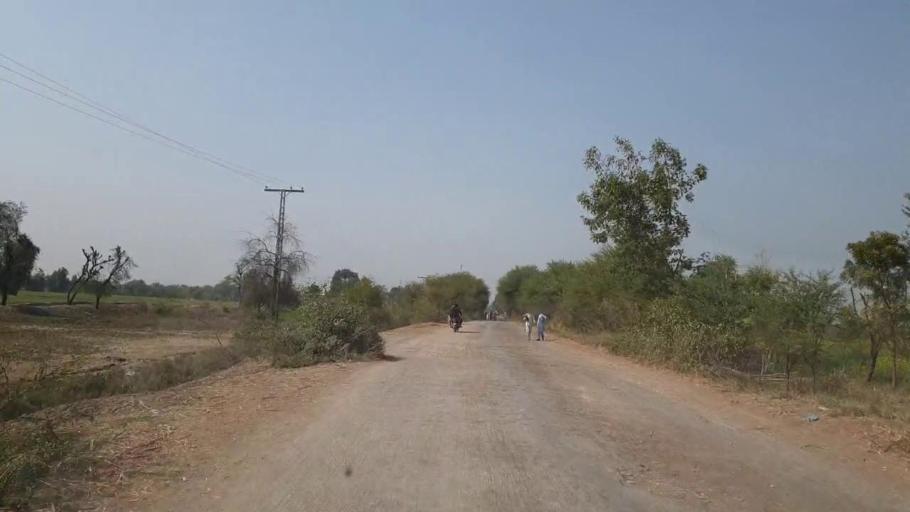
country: PK
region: Sindh
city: Mirpur Khas
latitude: 25.7035
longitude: 69.1364
